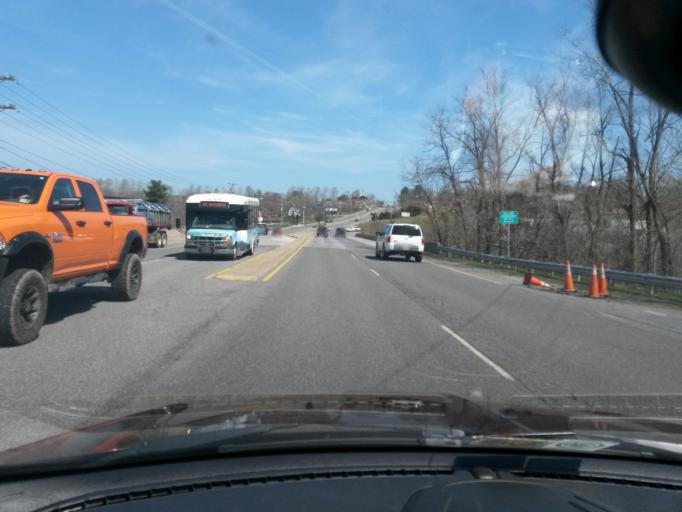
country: US
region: Virginia
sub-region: Montgomery County
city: Christiansburg
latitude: 37.1392
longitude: -80.4145
